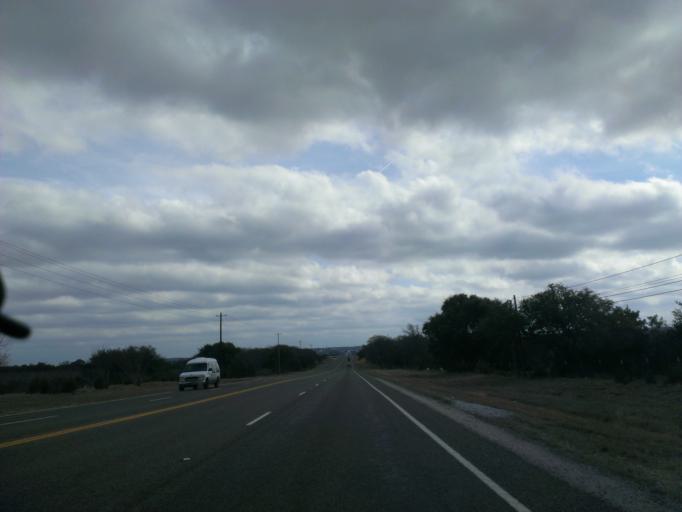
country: US
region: Texas
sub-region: Burnet County
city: Marble Falls
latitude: 30.4770
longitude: -98.1895
